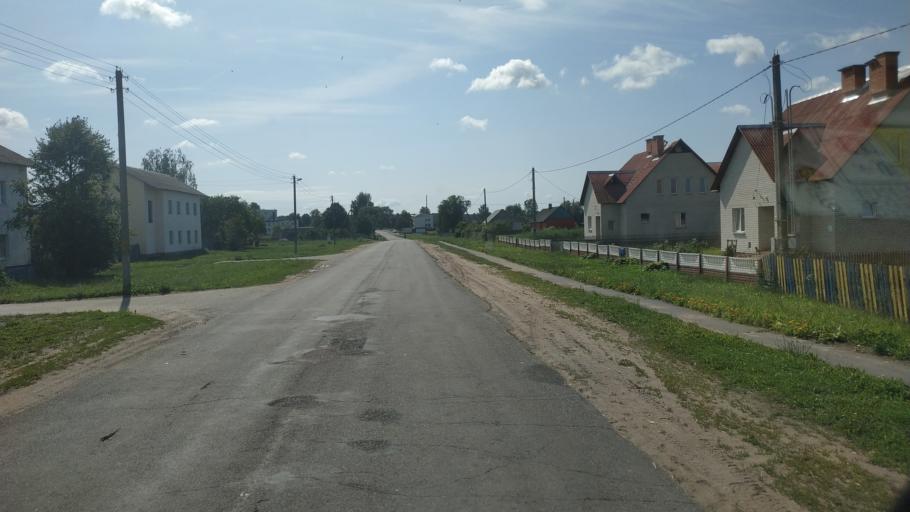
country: BY
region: Mogilev
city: Poselok Voskhod
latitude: 53.7070
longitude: 30.5021
